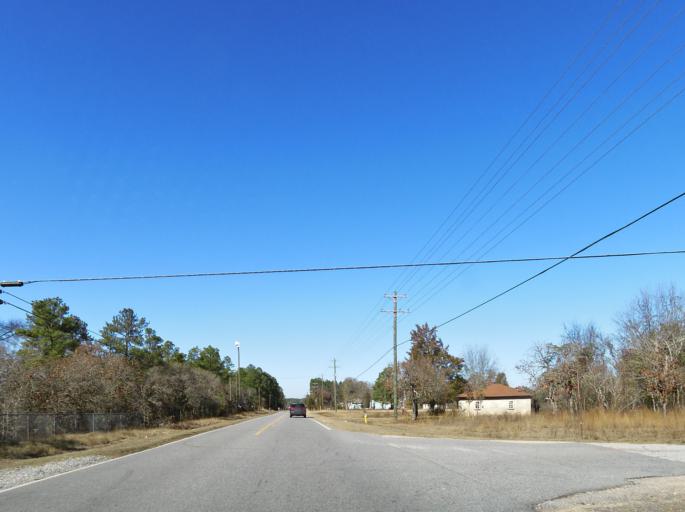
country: US
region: Georgia
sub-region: Bibb County
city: West Point
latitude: 32.7784
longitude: -83.7841
